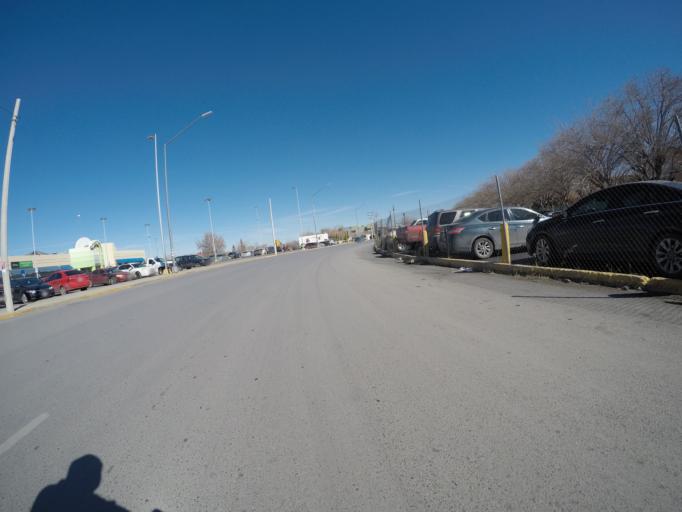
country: MX
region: Chihuahua
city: Ciudad Juarez
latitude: 31.7403
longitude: -106.4511
